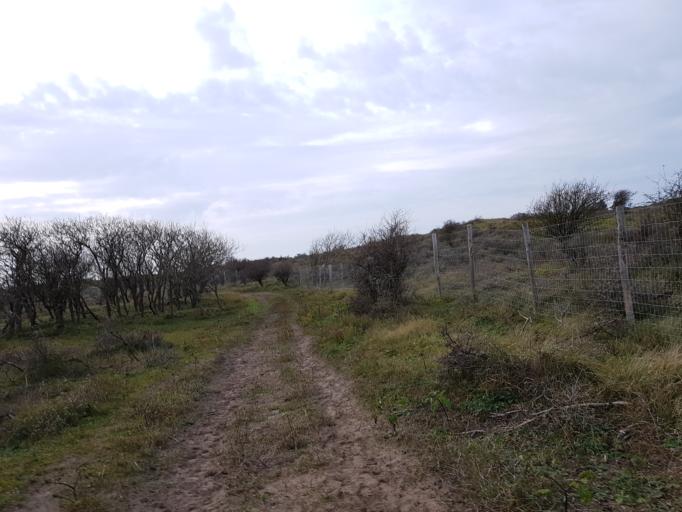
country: NL
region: North Holland
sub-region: Gemeente Zandvoort
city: Zandvoort
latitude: 52.3234
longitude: 4.5050
